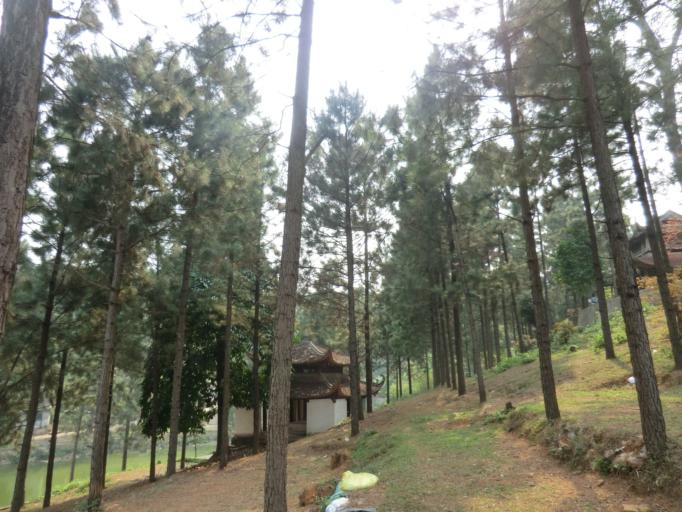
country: VN
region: Ha Noi
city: Chuc Son
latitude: 20.9500
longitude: 105.6804
